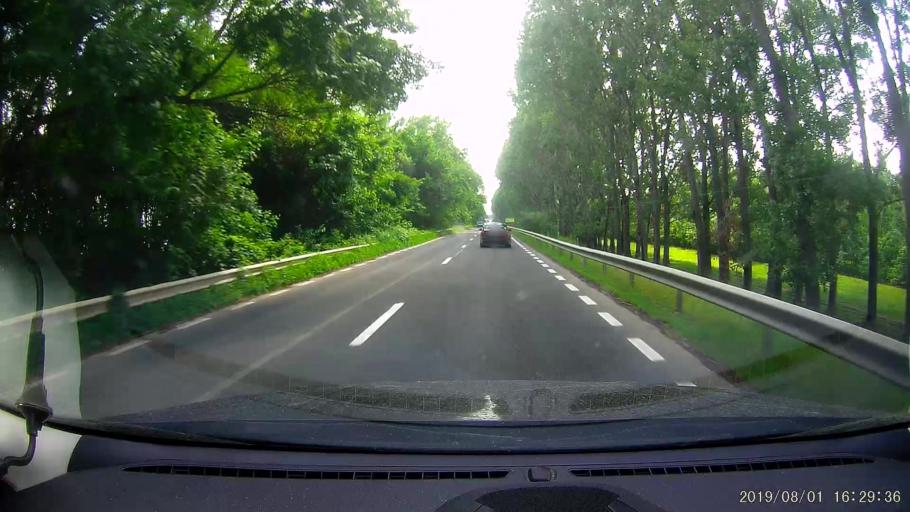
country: BG
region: Silistra
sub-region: Obshtina Silistra
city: Silistra
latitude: 44.1397
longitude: 27.2872
